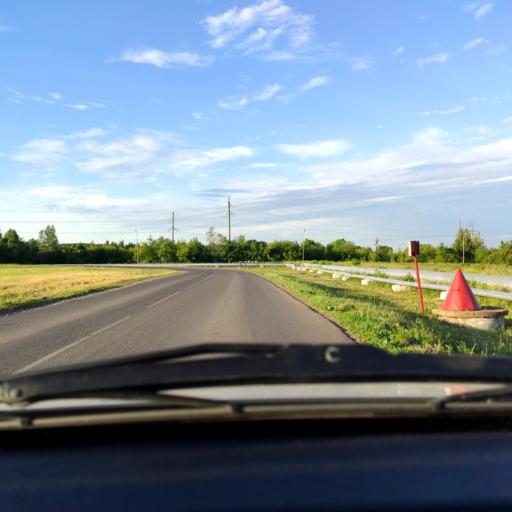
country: RU
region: Bashkortostan
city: Blagoveshchensk
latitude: 54.9102
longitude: 56.0538
